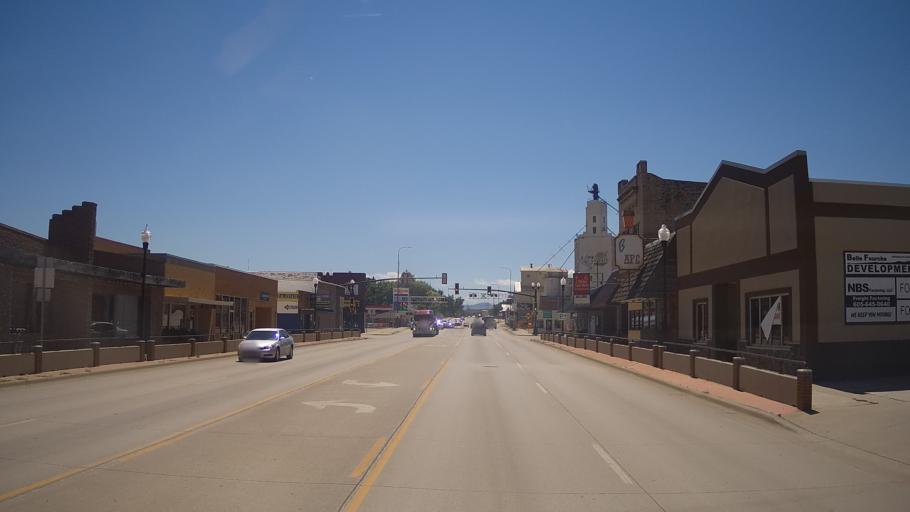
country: US
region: South Dakota
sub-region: Butte County
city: Belle Fourche
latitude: 44.6724
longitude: -103.8536
